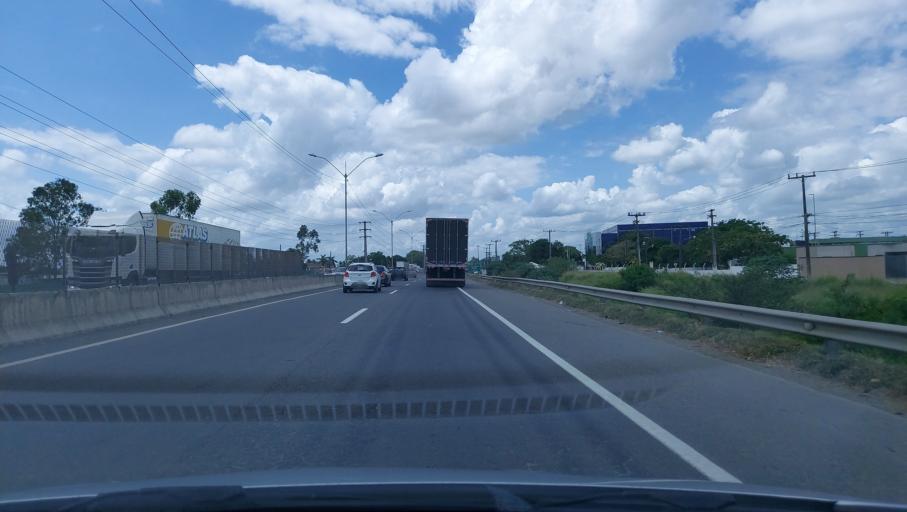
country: BR
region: Bahia
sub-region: Feira De Santana
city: Feira de Santana
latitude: -12.2758
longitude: -38.9384
